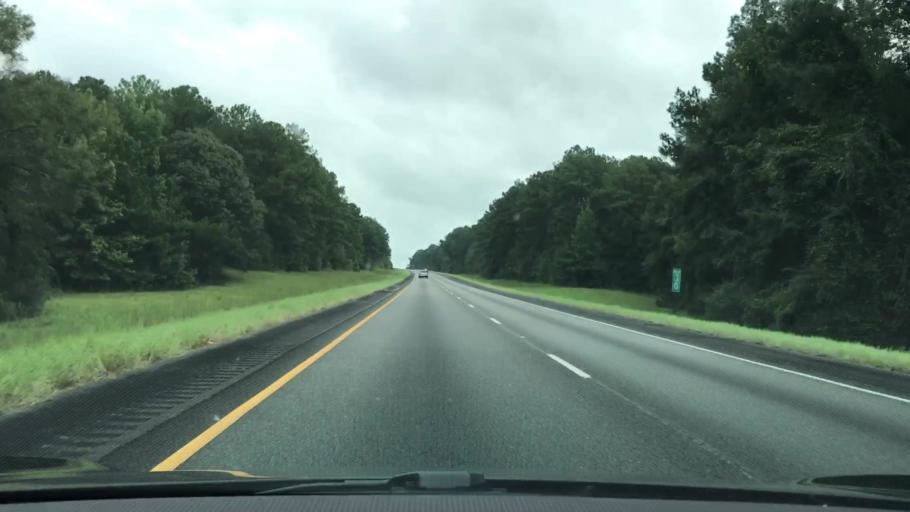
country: US
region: Alabama
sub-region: Elmore County
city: Tallassee
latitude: 32.4398
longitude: -85.8346
